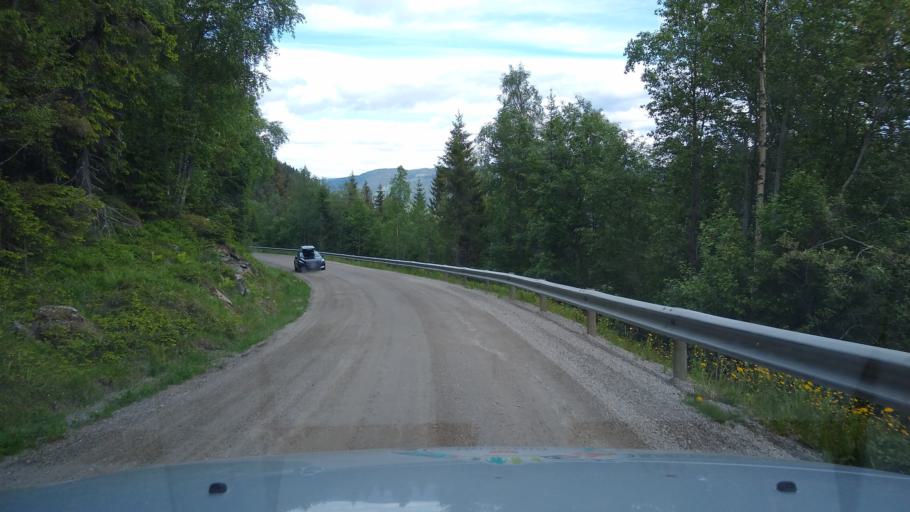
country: NO
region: Oppland
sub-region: Ringebu
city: Ringebu
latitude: 61.4976
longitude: 10.1437
